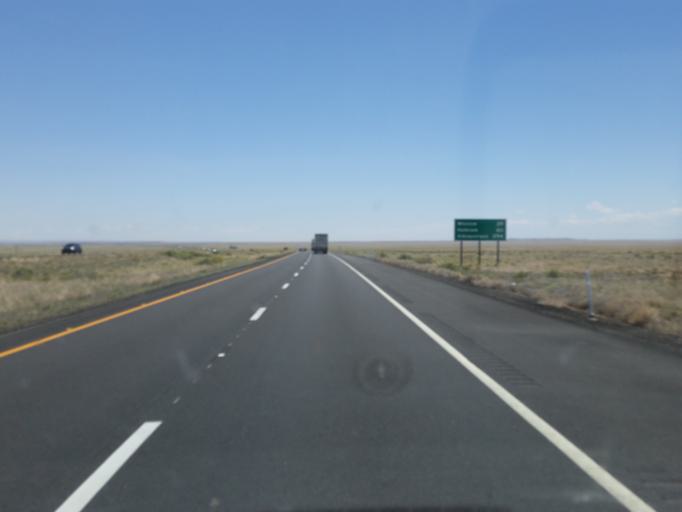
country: US
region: Arizona
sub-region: Coconino County
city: LeChee
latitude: 35.1242
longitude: -111.1709
